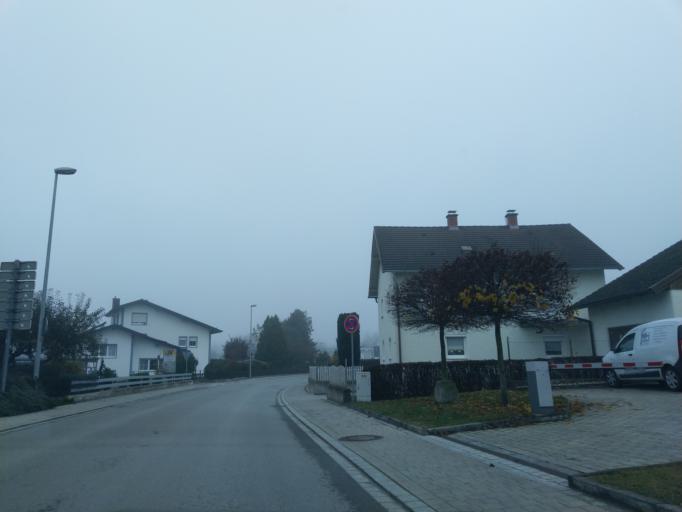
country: DE
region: Bavaria
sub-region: Lower Bavaria
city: Hengersberg
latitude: 48.7785
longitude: 13.0516
